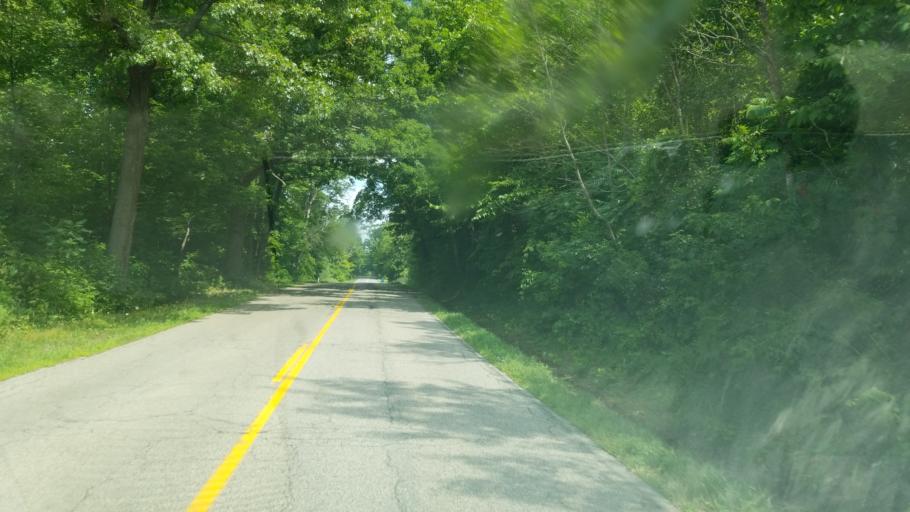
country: US
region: Michigan
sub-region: Kent County
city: Cedar Springs
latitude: 43.2480
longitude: -85.5112
